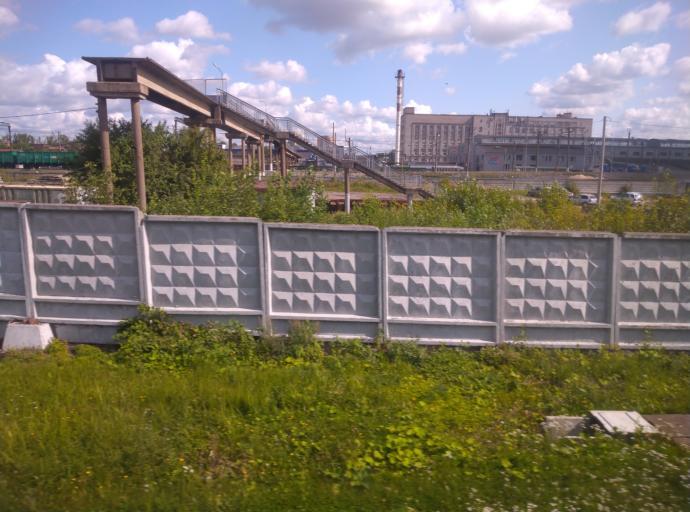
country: RU
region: St.-Petersburg
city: Obukhovo
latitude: 59.8779
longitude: 30.4092
